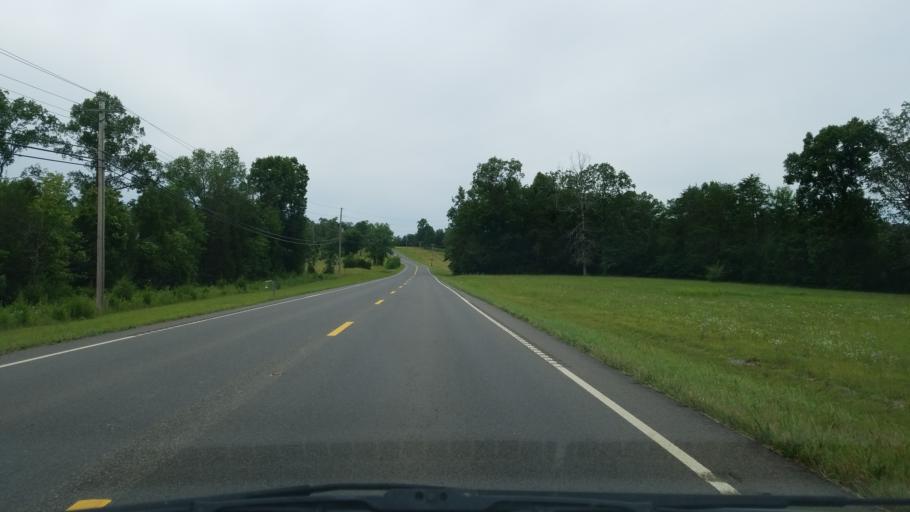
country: US
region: Tennessee
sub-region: Bradley County
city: Hopewell
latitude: 35.3142
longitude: -84.9492
